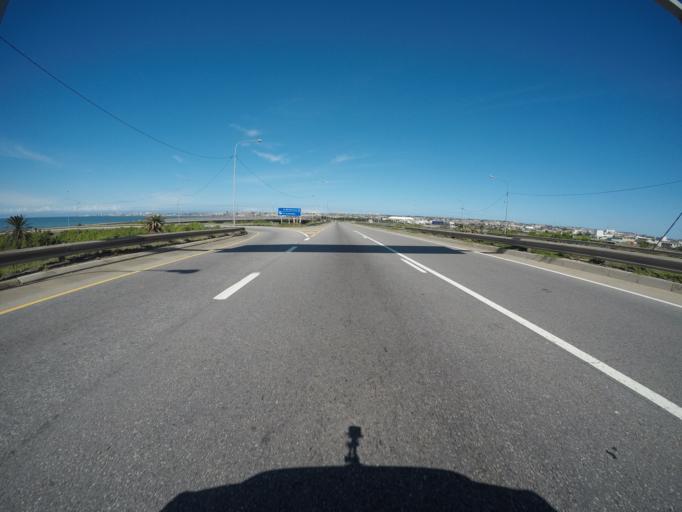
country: ZA
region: Eastern Cape
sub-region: Nelson Mandela Bay Metropolitan Municipality
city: Port Elizabeth
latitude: -33.9157
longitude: 25.6114
